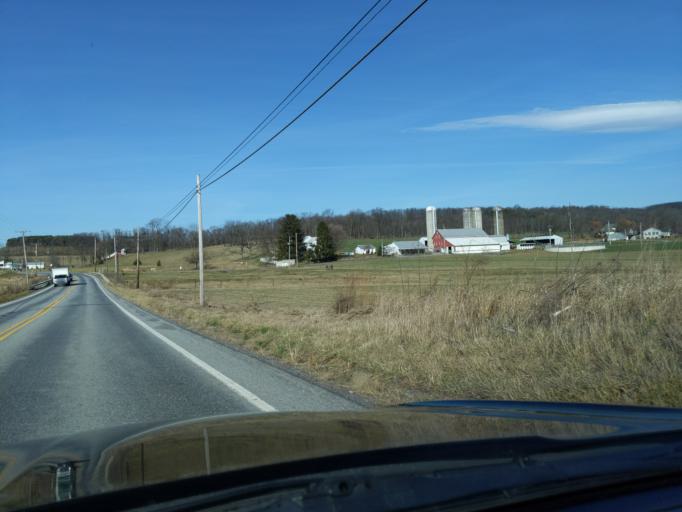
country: US
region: Pennsylvania
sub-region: Blair County
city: Martinsburg
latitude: 40.3099
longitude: -78.2969
